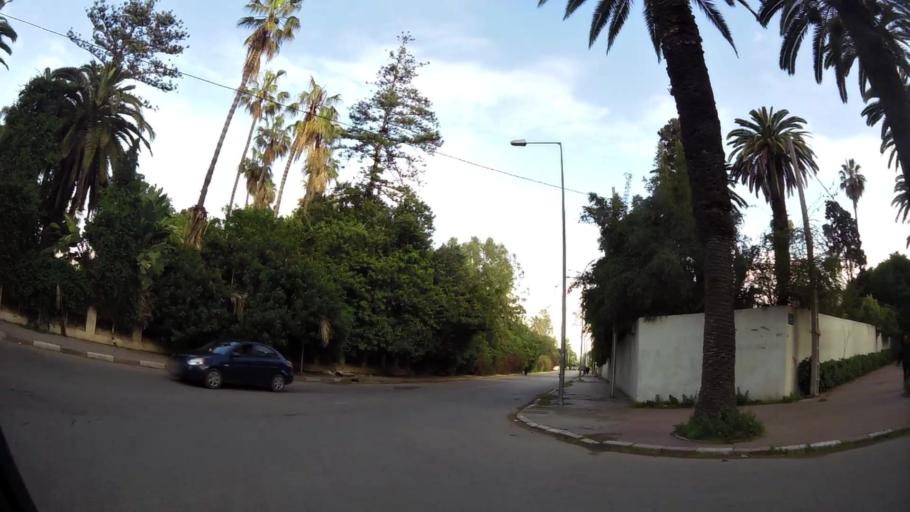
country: MA
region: Grand Casablanca
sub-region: Mohammedia
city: Mohammedia
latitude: 33.7066
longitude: -7.3949
